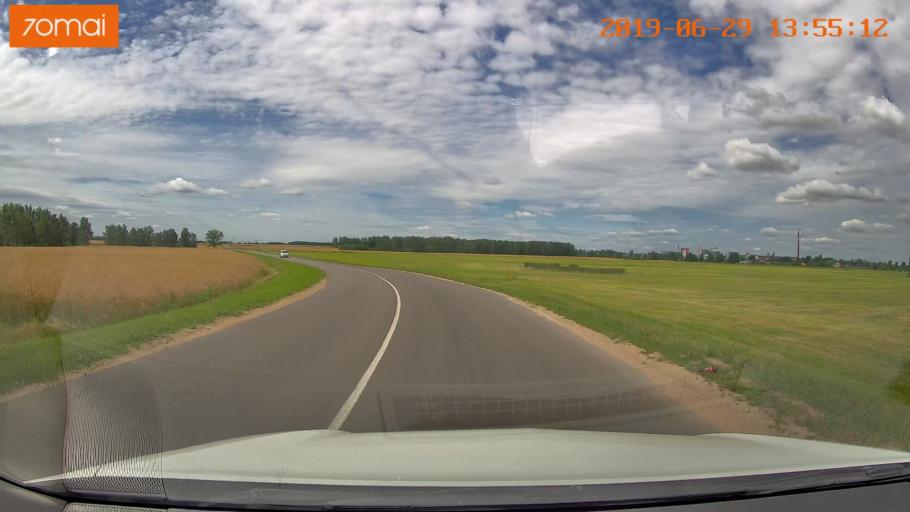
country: BY
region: Minsk
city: Slutsk
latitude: 52.9833
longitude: 27.5242
